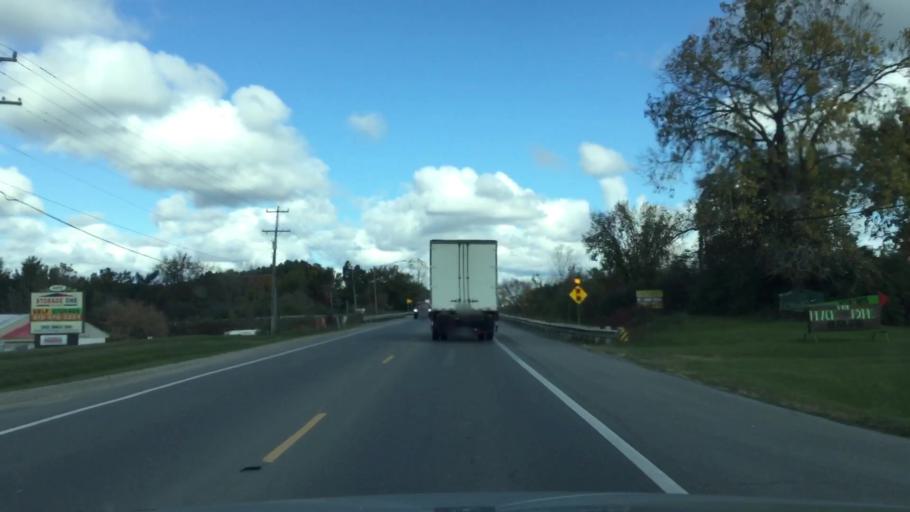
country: US
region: Michigan
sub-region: Lapeer County
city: Lapeer
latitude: 42.9398
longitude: -83.3134
